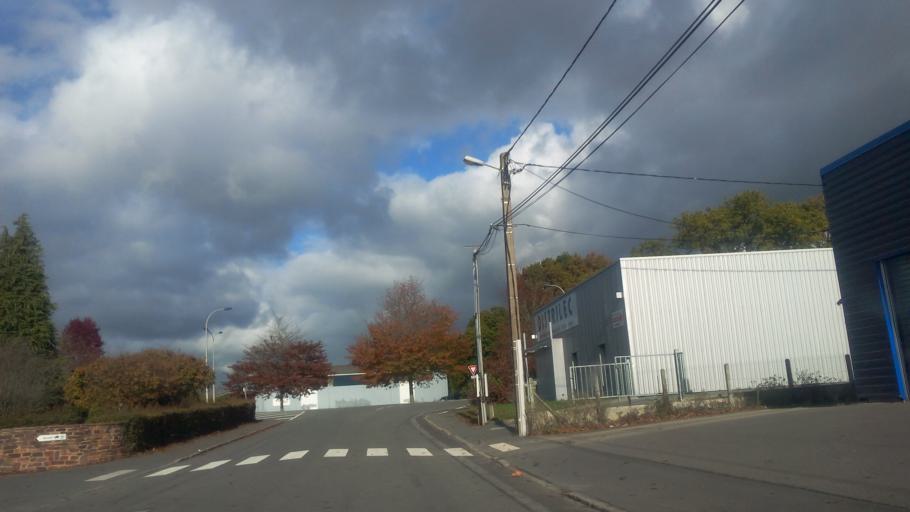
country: FR
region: Brittany
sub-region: Departement d'Ille-et-Vilaine
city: Redon
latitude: 47.6665
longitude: -2.0752
